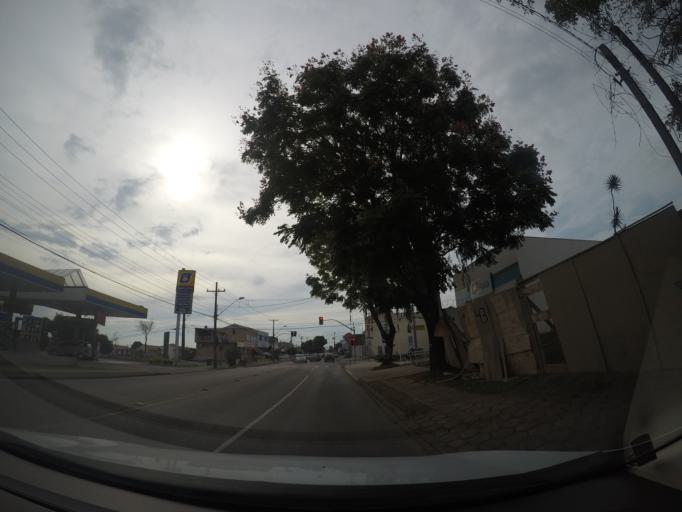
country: BR
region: Parana
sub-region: Sao Jose Dos Pinhais
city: Sao Jose dos Pinhais
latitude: -25.5058
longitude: -49.2643
